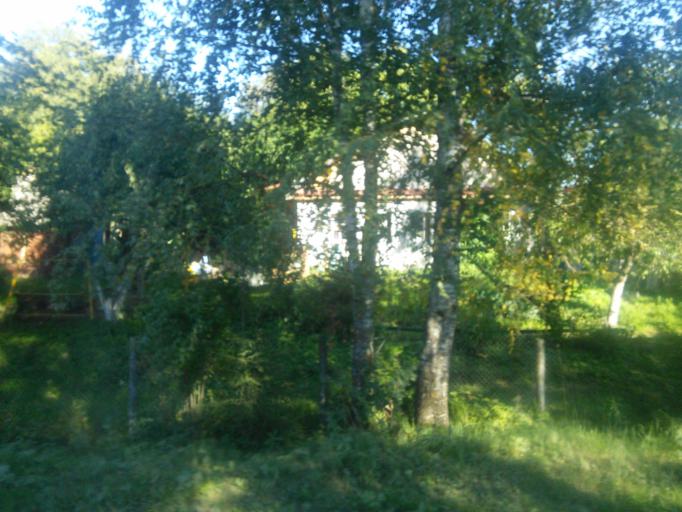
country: RU
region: Tverskaya
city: Kesova Gora
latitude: 57.5917
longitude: 37.2915
